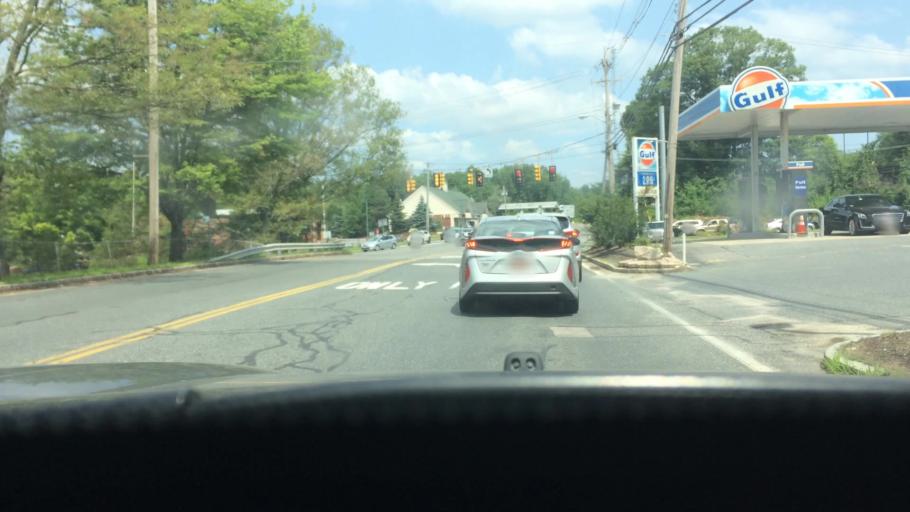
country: US
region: Massachusetts
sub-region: Worcester County
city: Milford
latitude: 42.1612
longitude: -71.5081
